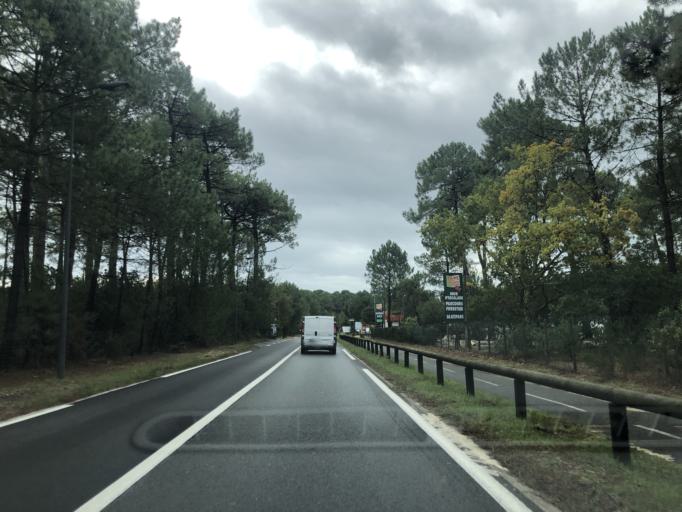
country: FR
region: Aquitaine
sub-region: Departement de la Gironde
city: Ares
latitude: 44.7327
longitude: -1.1963
